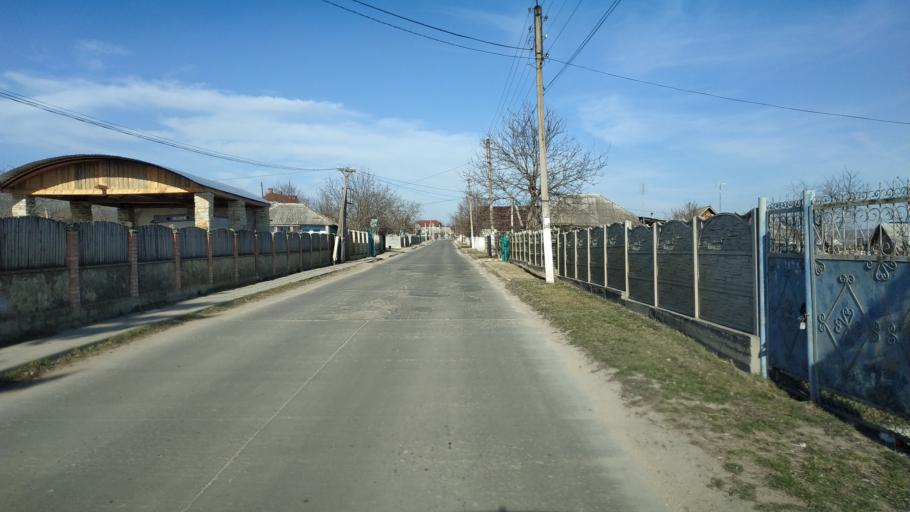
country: MD
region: Chisinau
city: Vatra
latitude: 47.0107
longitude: 28.6634
